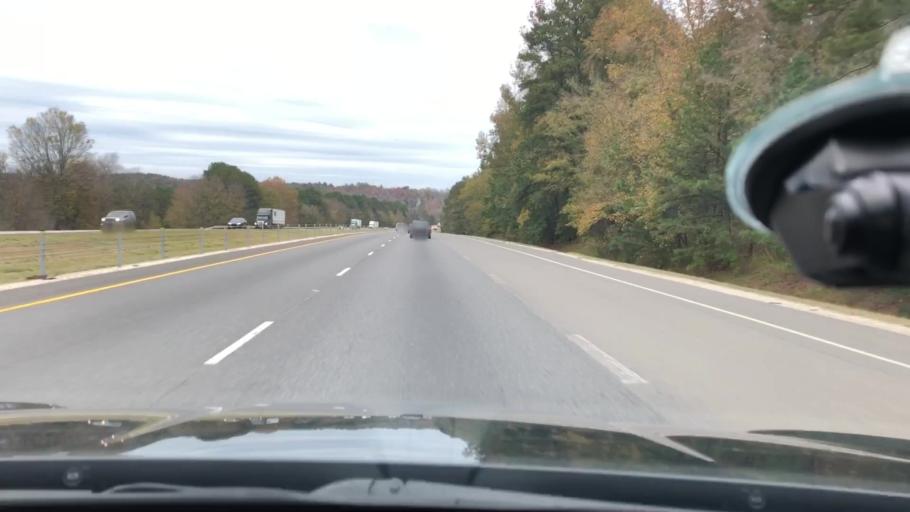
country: US
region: Arkansas
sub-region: Hot Spring County
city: Malvern
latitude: 34.3357
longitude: -92.9162
